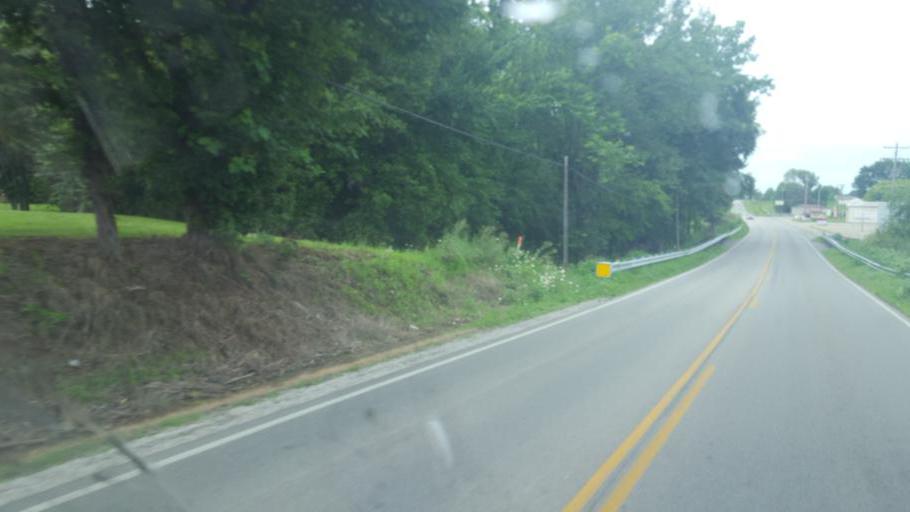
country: US
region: Ohio
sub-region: Pickaway County
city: Circleville
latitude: 39.6374
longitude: -82.9472
